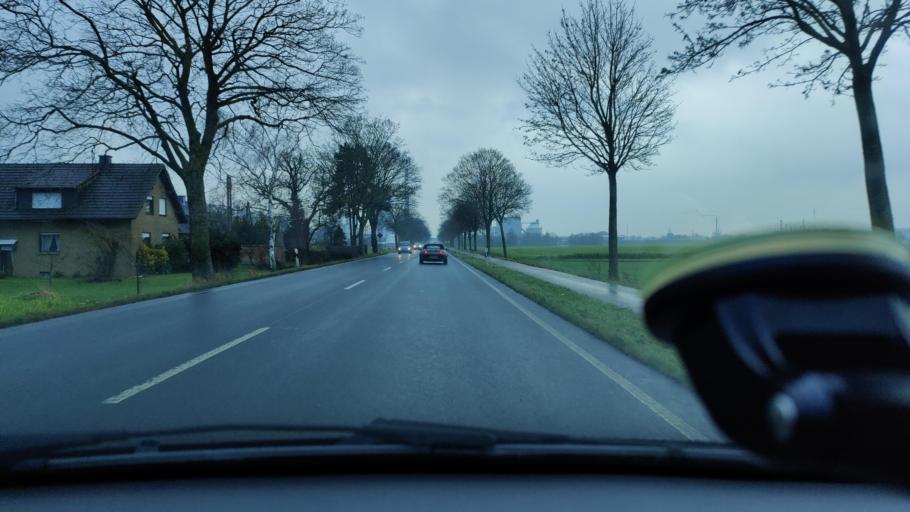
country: DE
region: North Rhine-Westphalia
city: Rheinberg
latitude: 51.5704
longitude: 6.5694
